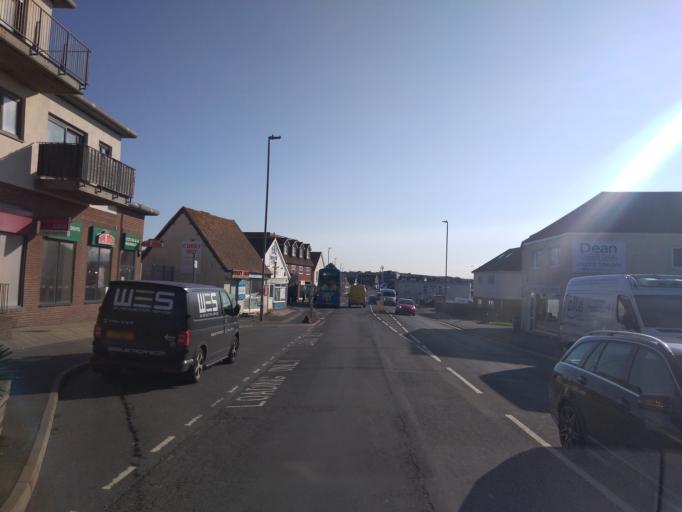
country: GB
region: England
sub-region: East Sussex
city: Peacehaven
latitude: 50.7911
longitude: 0.0005
